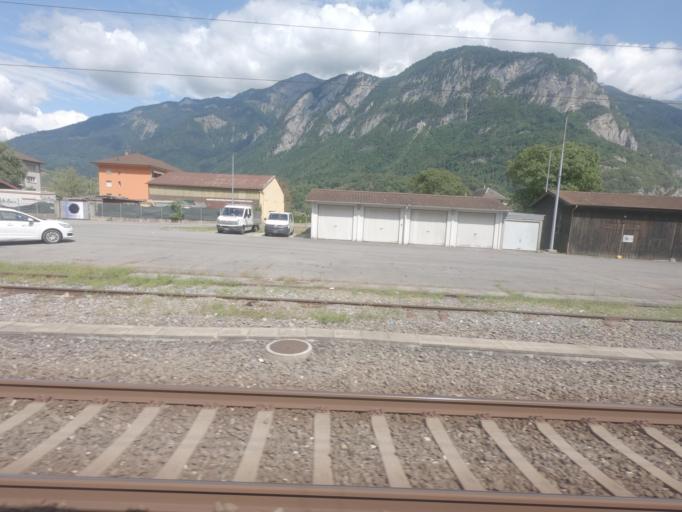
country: CH
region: Valais
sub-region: Saint-Maurice District
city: Saint-Maurice
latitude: 46.2137
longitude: 7.0022
